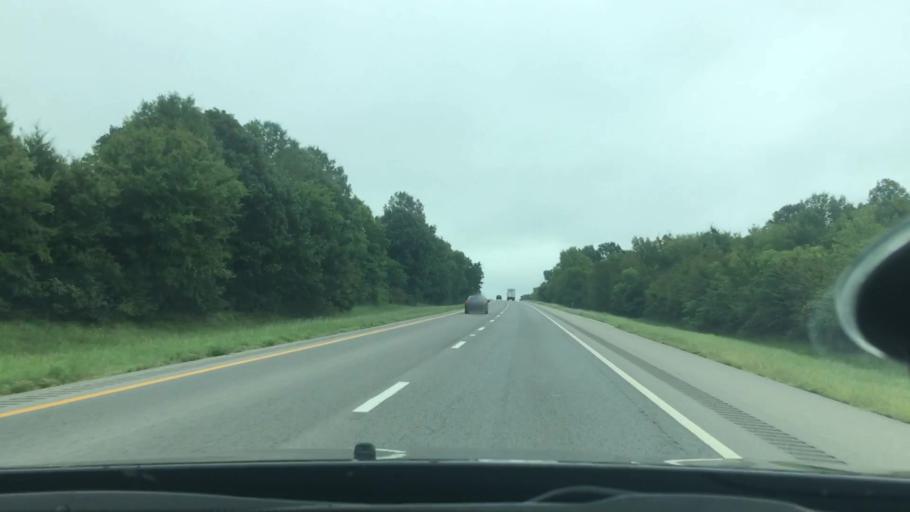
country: US
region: Oklahoma
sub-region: Muskogee County
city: Warner
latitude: 35.4564
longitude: -95.3919
